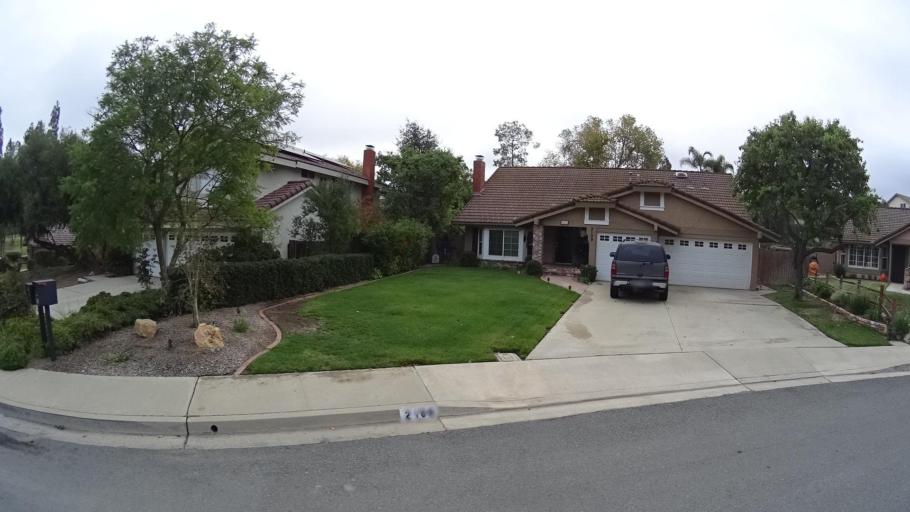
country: US
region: California
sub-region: San Diego County
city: Rancho San Diego
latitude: 32.7510
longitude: -116.9176
